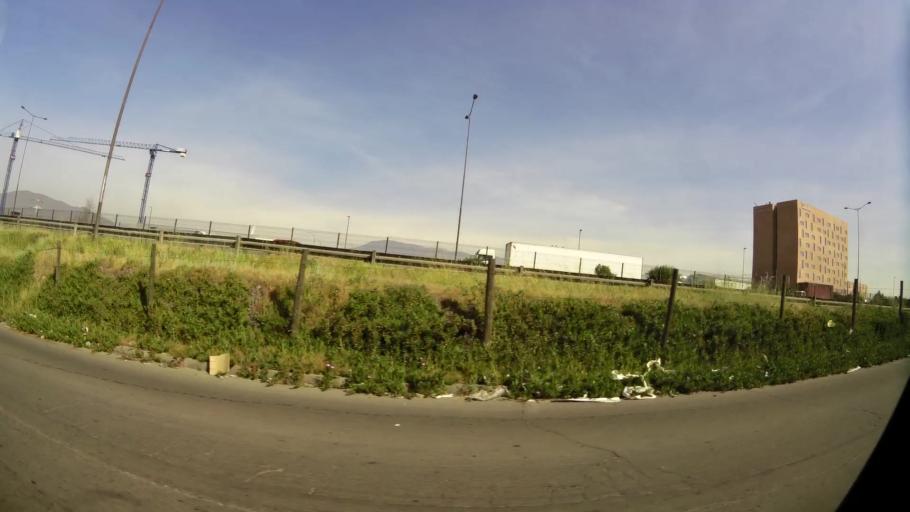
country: CL
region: Santiago Metropolitan
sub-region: Provincia de Santiago
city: Lo Prado
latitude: -33.4301
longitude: -70.7840
